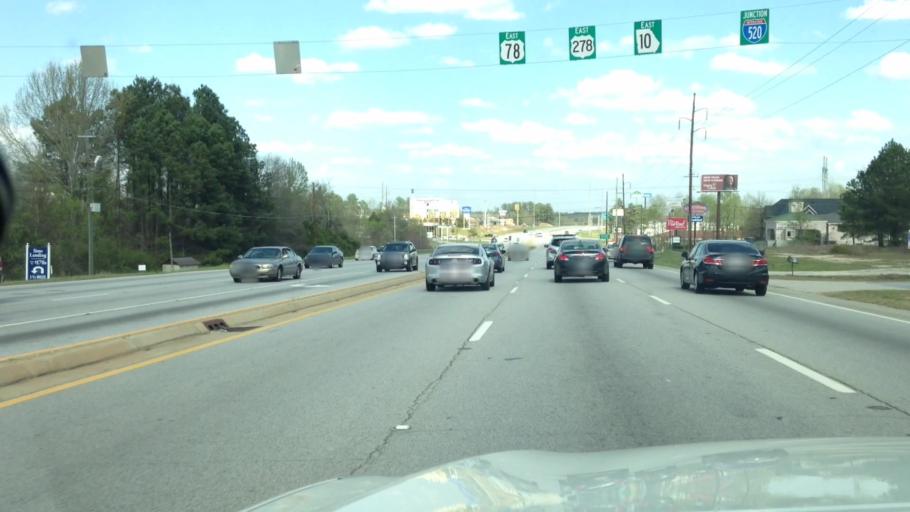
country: US
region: Georgia
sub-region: Columbia County
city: Martinez
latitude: 33.4478
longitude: -82.0851
